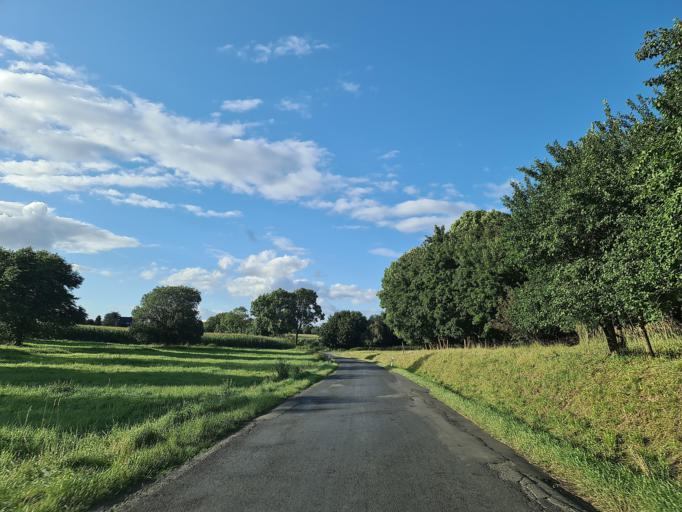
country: DE
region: Saxony
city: Syrau
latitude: 50.5341
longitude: 12.0825
